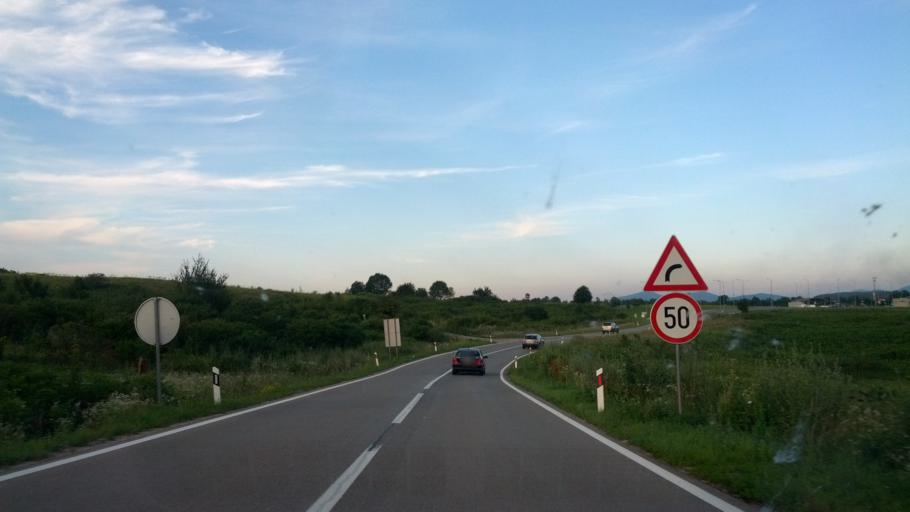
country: BA
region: Federation of Bosnia and Herzegovina
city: Izacic
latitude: 44.8773
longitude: 15.7567
